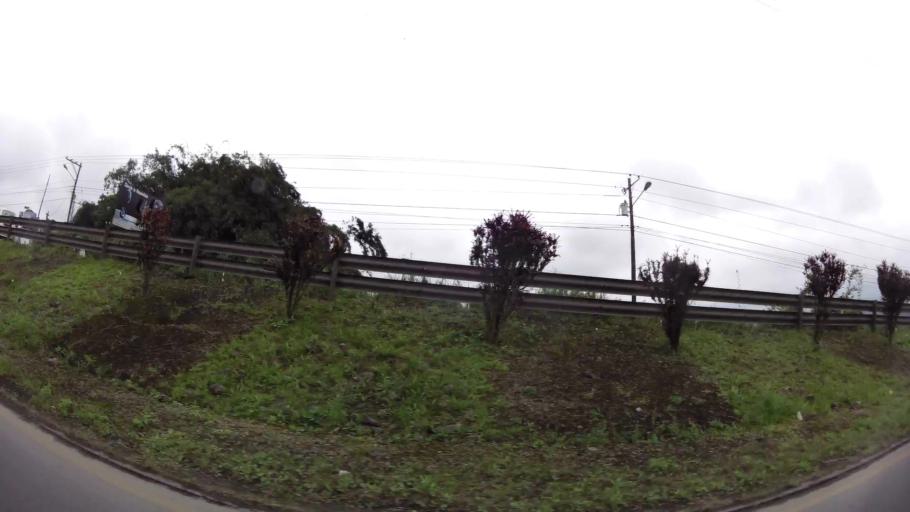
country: EC
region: Santo Domingo de los Tsachilas
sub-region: Canton Santo Domingo de los Colorados
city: Santo Domingo de los Colorados
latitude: -0.2471
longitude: -79.1446
